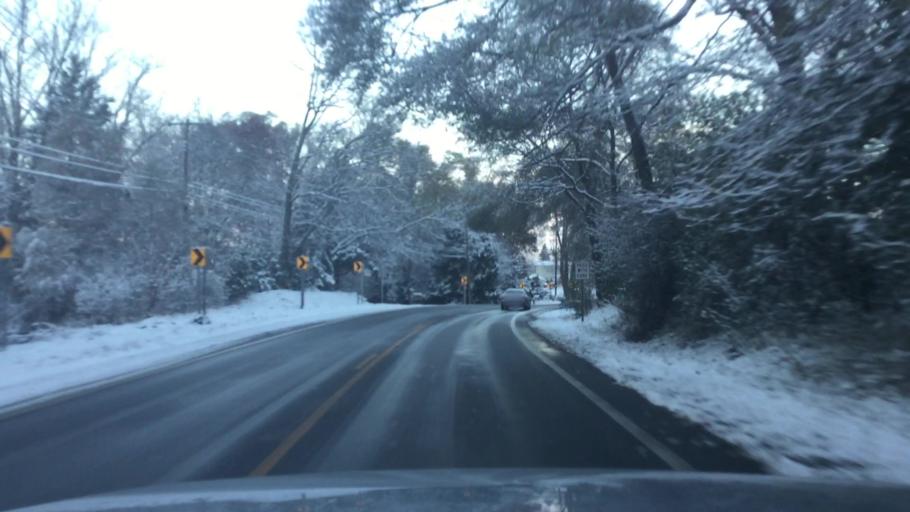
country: US
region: Michigan
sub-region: Oakland County
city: Wolverine Lake
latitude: 42.5917
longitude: -83.4378
